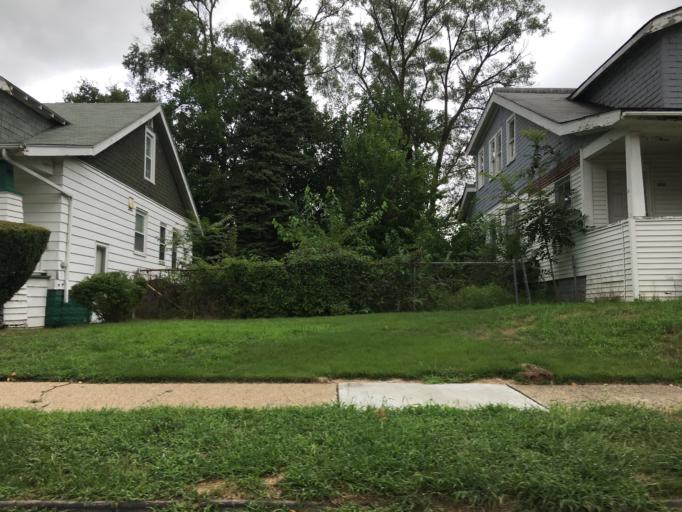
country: US
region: Michigan
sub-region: Oakland County
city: Ferndale
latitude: 42.4139
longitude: -83.1439
